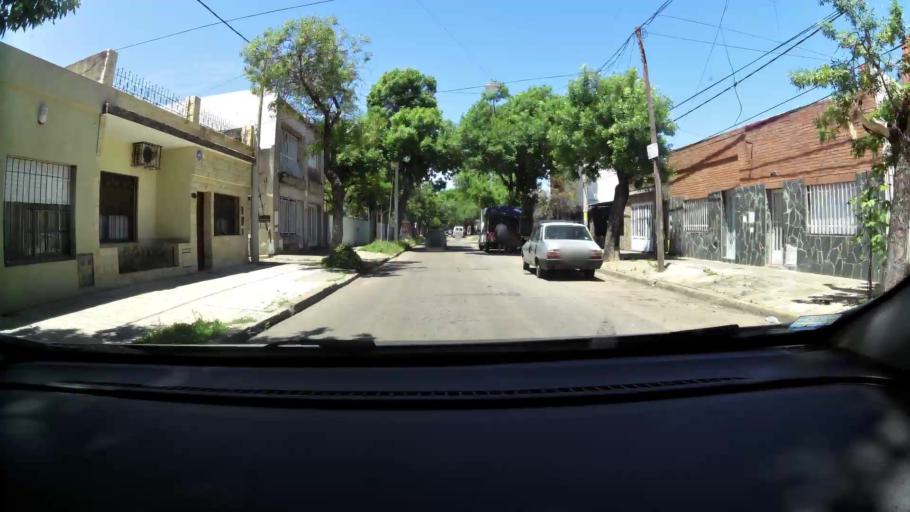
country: AR
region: Santa Fe
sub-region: Departamento de Rosario
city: Rosario
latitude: -32.9425
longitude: -60.7023
